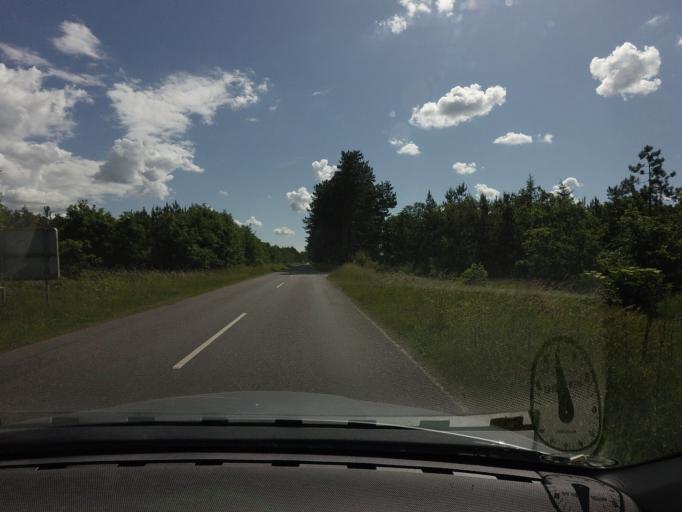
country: DK
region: Central Jutland
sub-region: Syddjurs Kommune
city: Ryomgard
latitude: 56.3558
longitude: 10.4939
